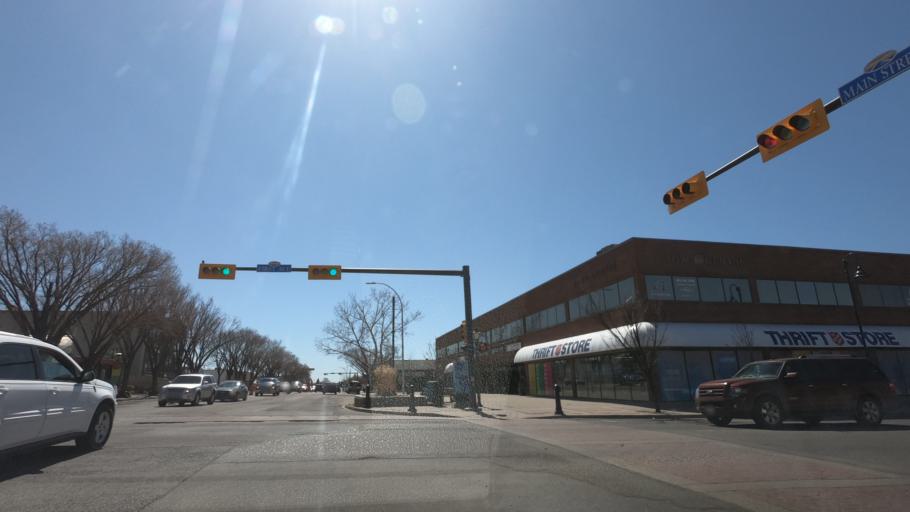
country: CA
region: Alberta
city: Airdrie
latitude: 51.2928
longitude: -114.0136
